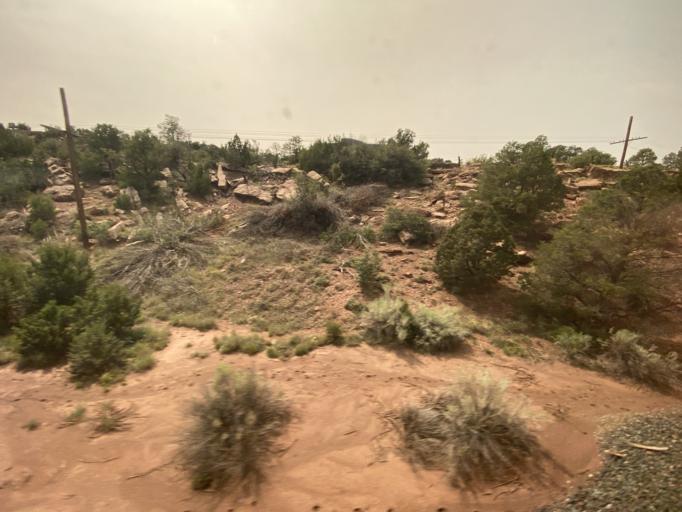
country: US
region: New Mexico
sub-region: San Miguel County
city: Pecos
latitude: 35.4018
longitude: -105.4958
